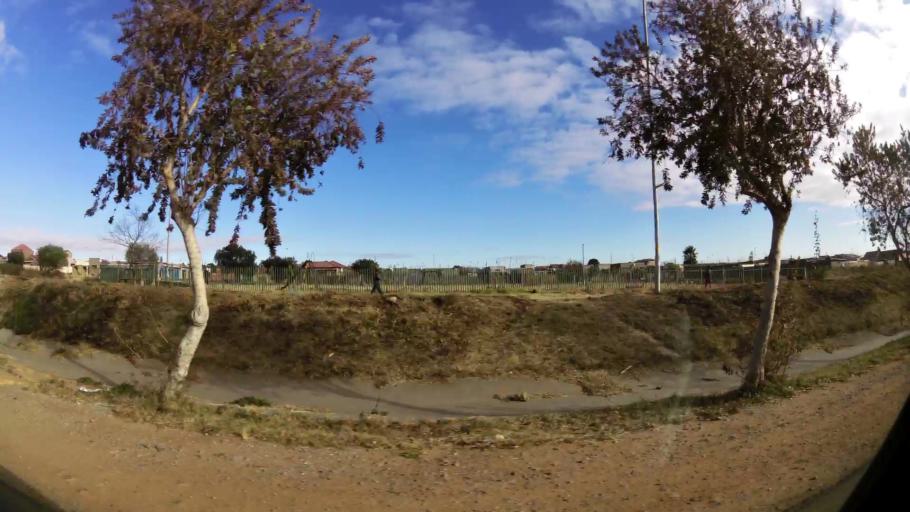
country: ZA
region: Gauteng
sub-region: City of Johannesburg Metropolitan Municipality
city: Modderfontein
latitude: -26.0430
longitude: 28.1881
